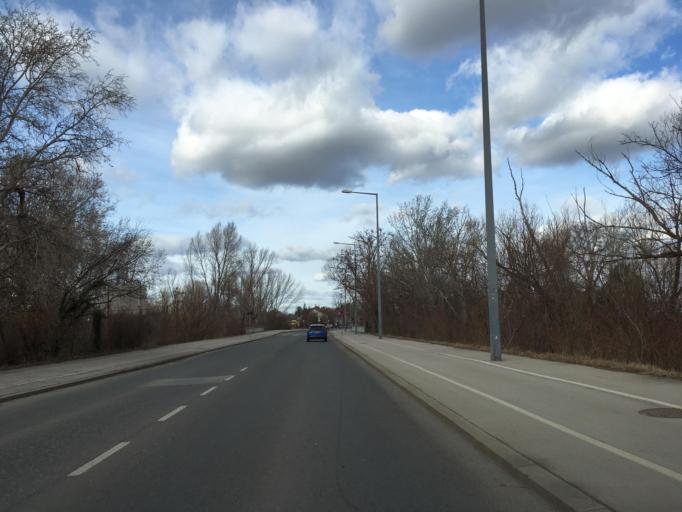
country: AT
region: Lower Austria
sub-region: Politischer Bezirk Wien-Umgebung
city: Schwechat
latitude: 48.2047
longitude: 16.4761
